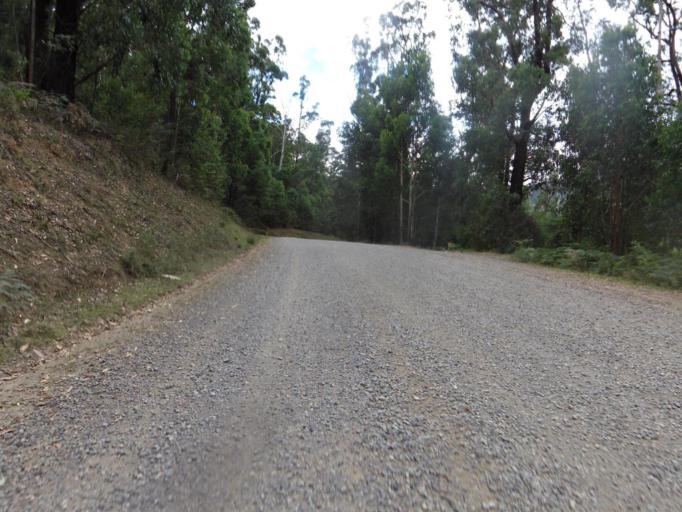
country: AU
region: Victoria
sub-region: Yarra Ranges
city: Healesville
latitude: -37.4072
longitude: 145.5588
